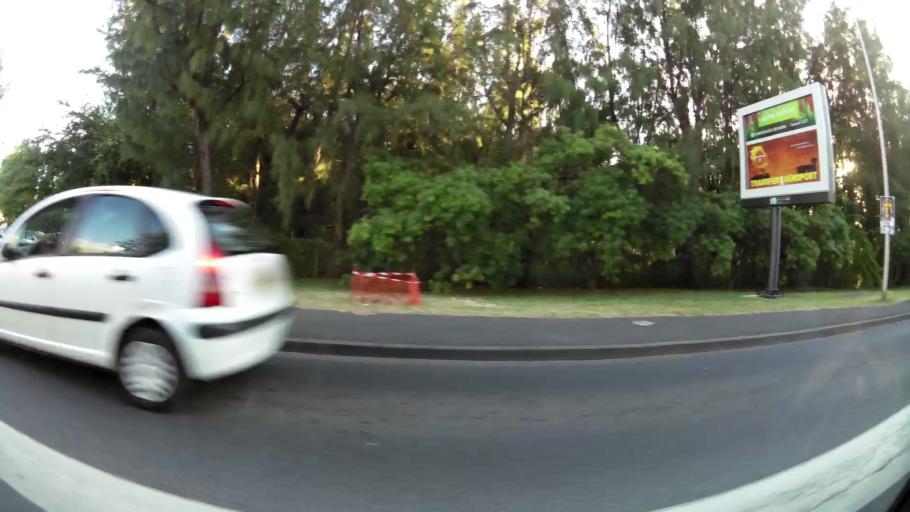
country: RE
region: Reunion
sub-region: Reunion
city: Trois-Bassins
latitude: -21.0917
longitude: 55.2355
